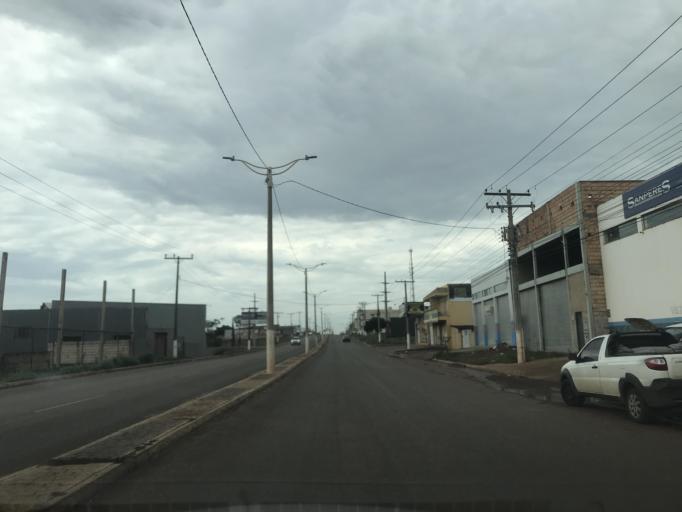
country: BR
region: Goias
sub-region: Luziania
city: Luziania
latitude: -16.2322
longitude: -47.9402
